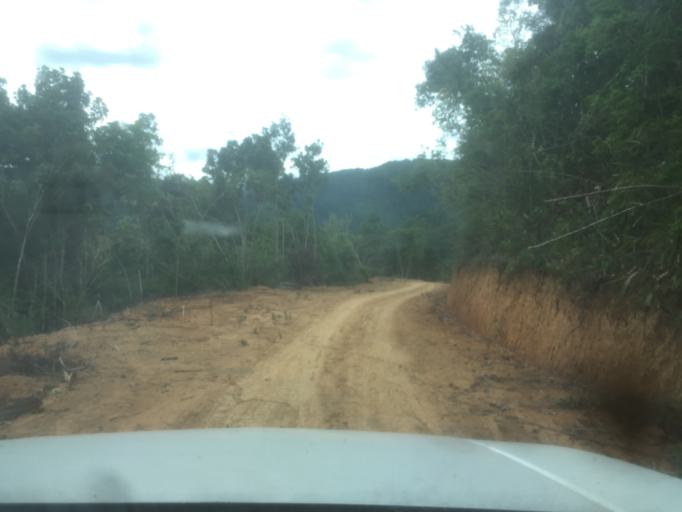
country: LA
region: Phongsali
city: Khoa
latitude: 20.9202
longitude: 102.5594
